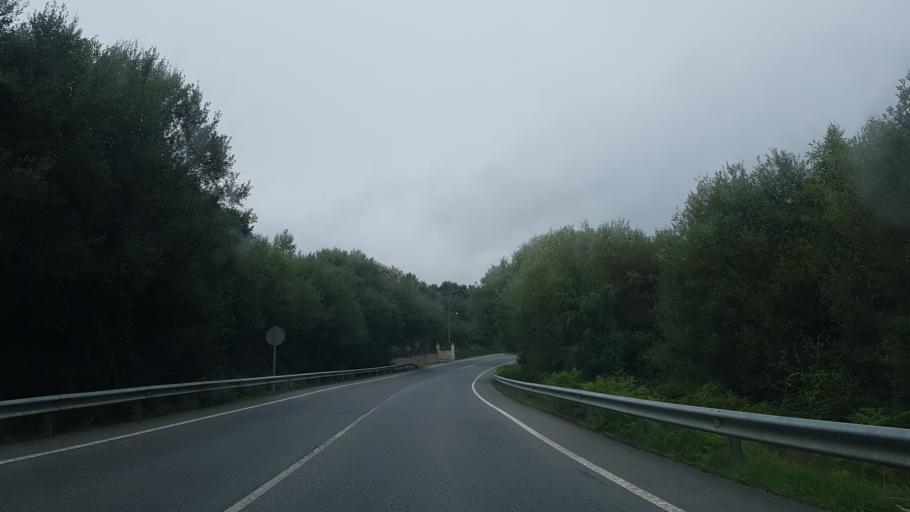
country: ES
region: Galicia
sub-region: Provincia de Lugo
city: Lugo
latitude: 42.9923
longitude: -7.5993
